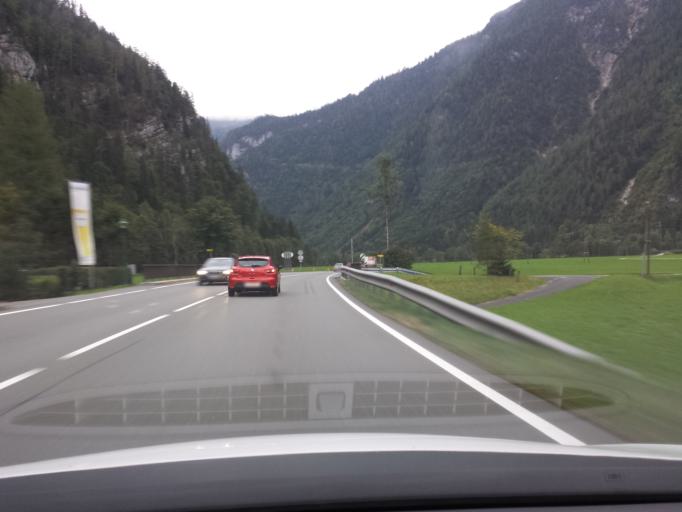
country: AT
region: Salzburg
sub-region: Politischer Bezirk Zell am See
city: Leogang
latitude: 47.5156
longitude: 12.7583
